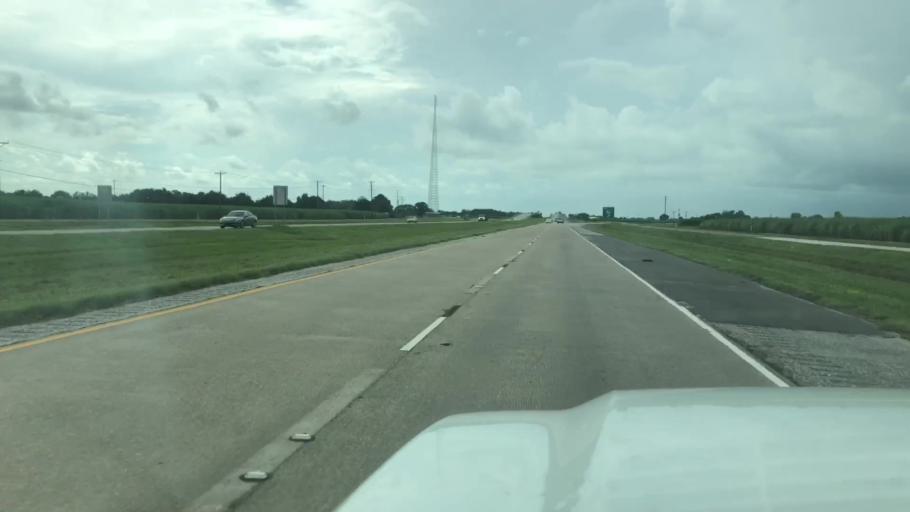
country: US
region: Louisiana
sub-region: Iberia Parish
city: Jeanerette
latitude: 29.9150
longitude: -91.7212
